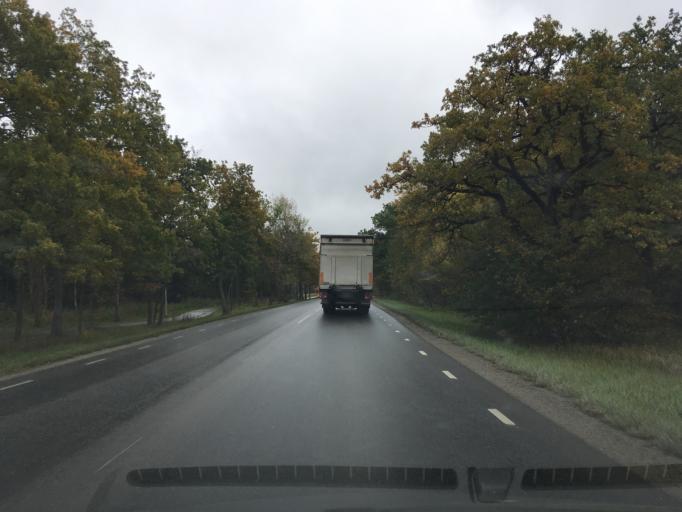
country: EE
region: Harju
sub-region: Saue vald
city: Laagri
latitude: 59.3762
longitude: 24.5824
